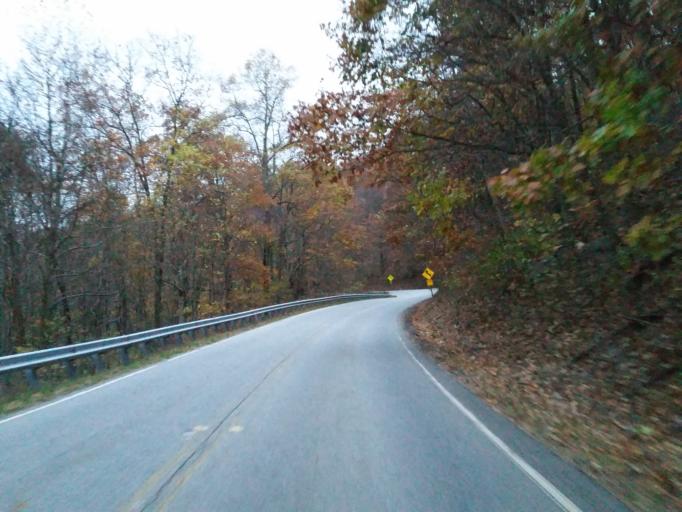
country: US
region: Georgia
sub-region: Lumpkin County
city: Dahlonega
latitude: 34.6799
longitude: -84.0027
